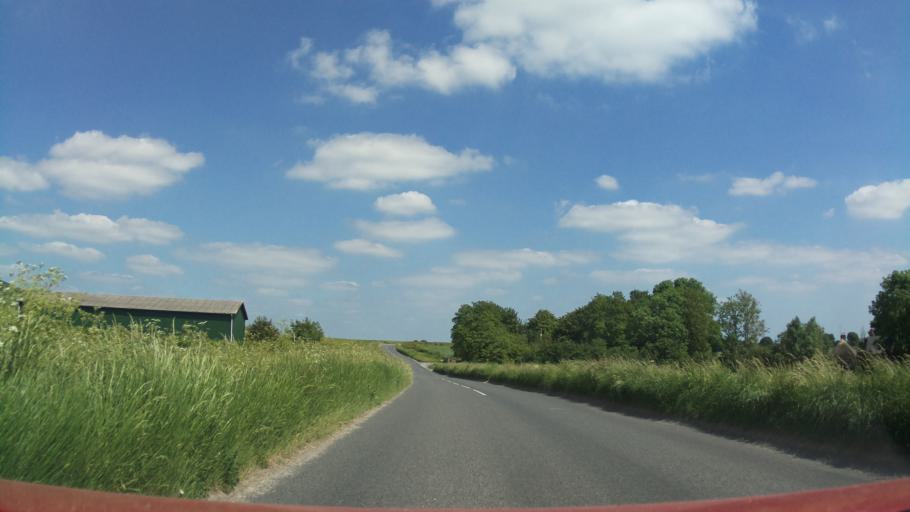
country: GB
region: England
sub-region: Wiltshire
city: Woodborough
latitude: 51.3630
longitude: -1.8689
